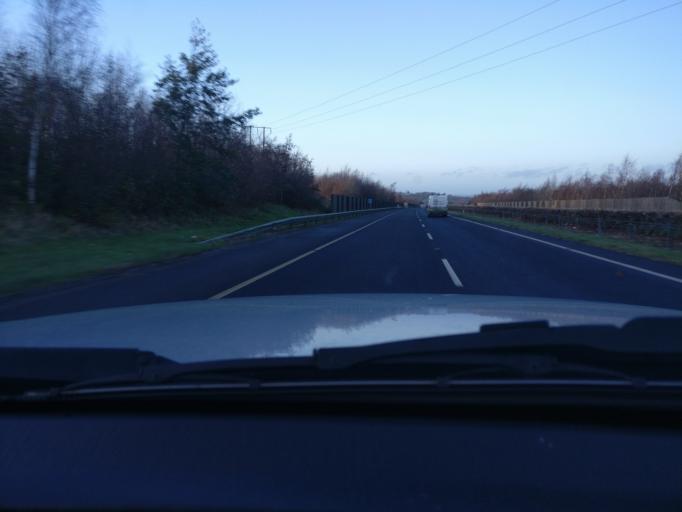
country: IE
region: Leinster
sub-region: Lu
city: Dundalk
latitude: 53.9856
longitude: -6.4334
